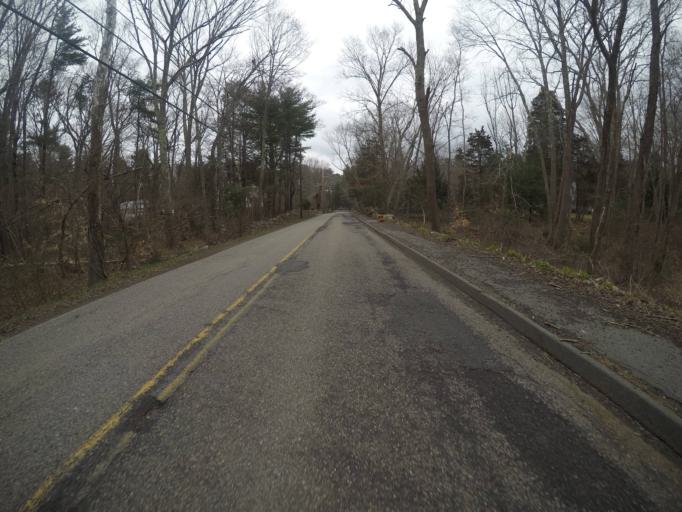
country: US
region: Massachusetts
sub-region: Bristol County
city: Easton
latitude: 42.0619
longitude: -71.1406
